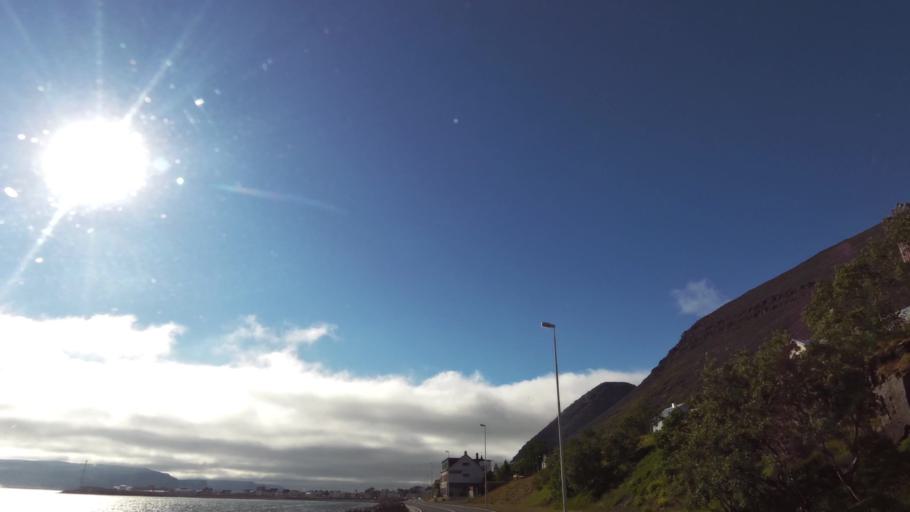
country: IS
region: West
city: Olafsvik
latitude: 65.5945
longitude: -23.9825
